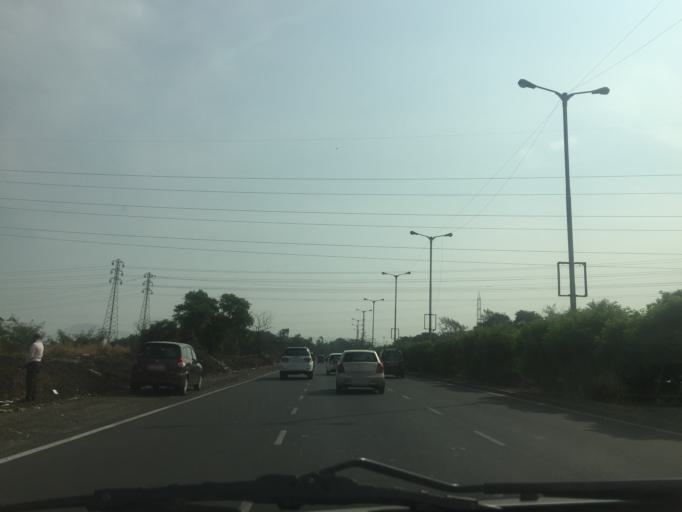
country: IN
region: Maharashtra
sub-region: Thane
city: Airoli
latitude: 19.1542
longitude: 72.9602
